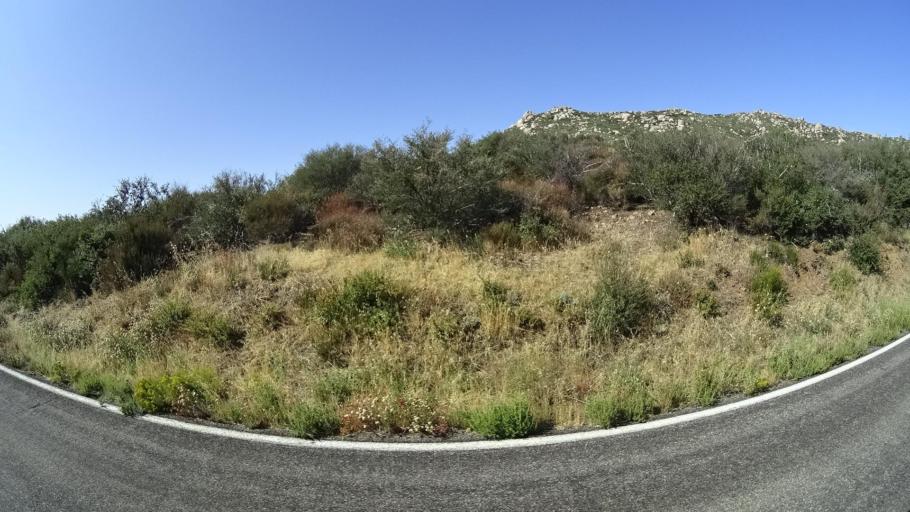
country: US
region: California
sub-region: San Diego County
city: Julian
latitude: 32.9710
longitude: -116.5140
